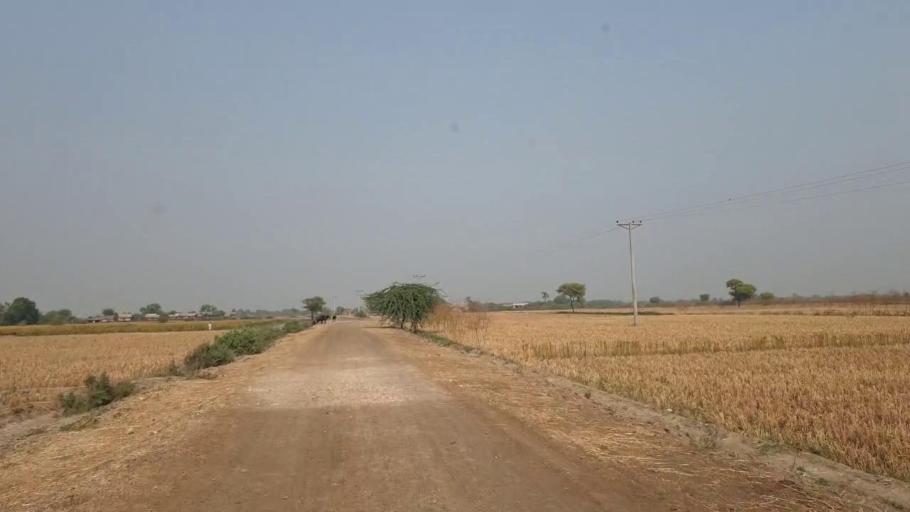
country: PK
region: Sindh
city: Matli
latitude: 25.1524
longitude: 68.7295
